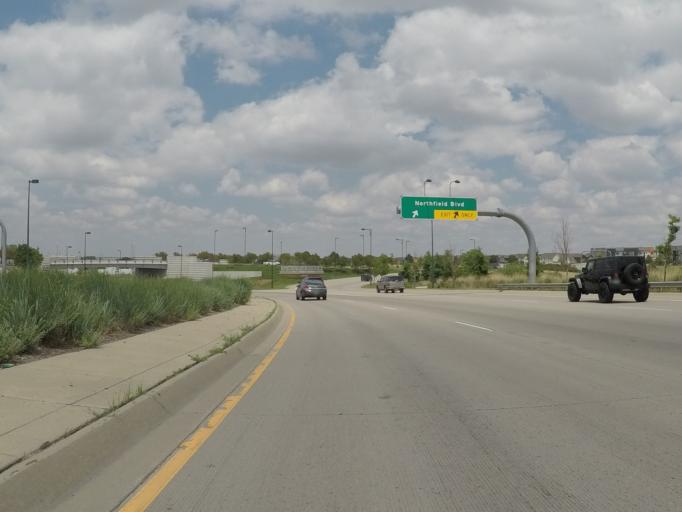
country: US
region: Colorado
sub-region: Adams County
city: Commerce City
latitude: 39.7840
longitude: -104.8999
